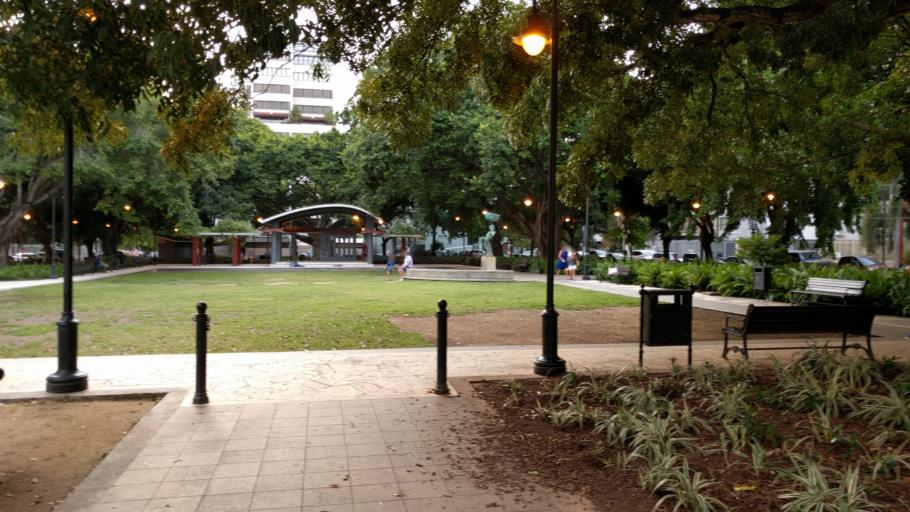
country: PR
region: San Juan
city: San Juan
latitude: 18.4539
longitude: -66.0697
